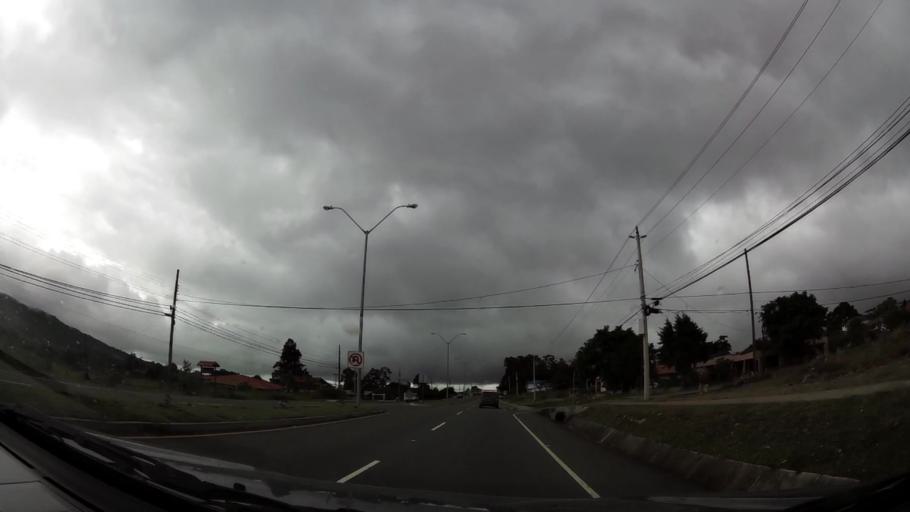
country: PA
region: Chiriqui
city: Palmira
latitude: 8.7496
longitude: -82.4323
